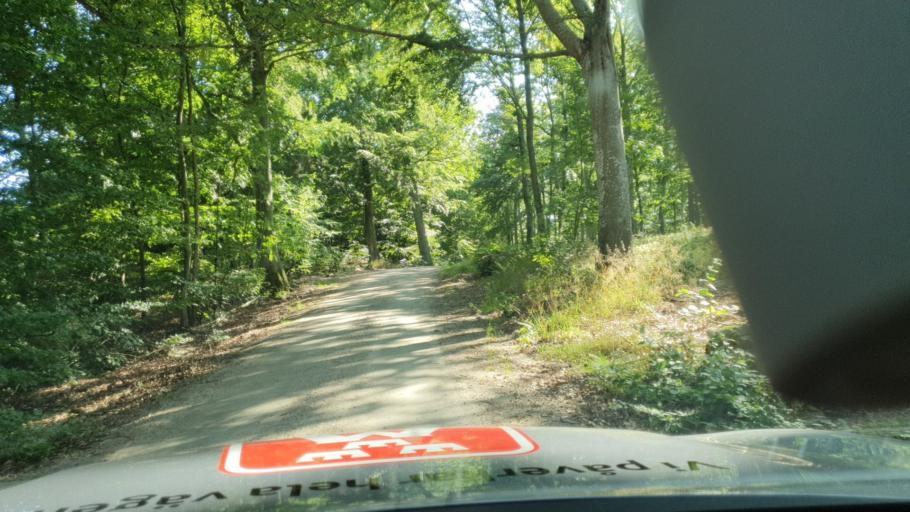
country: SE
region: Skane
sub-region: Bromolla Kommun
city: Nasum
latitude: 56.1517
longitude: 14.4602
